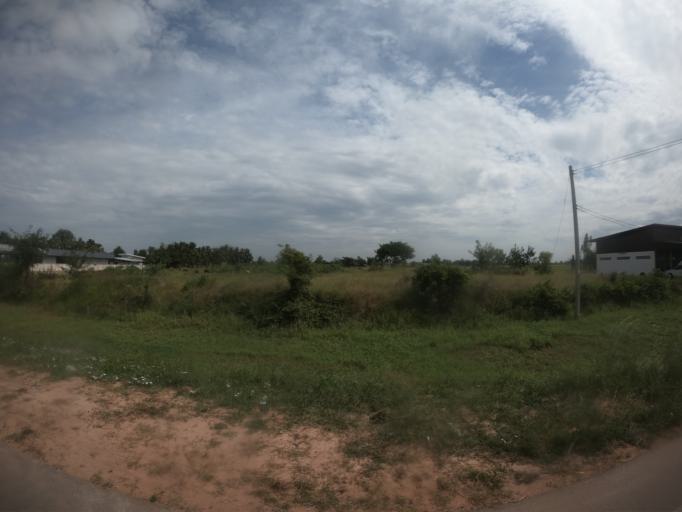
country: TH
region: Maha Sarakham
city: Chiang Yuen
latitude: 16.3839
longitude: 103.1030
